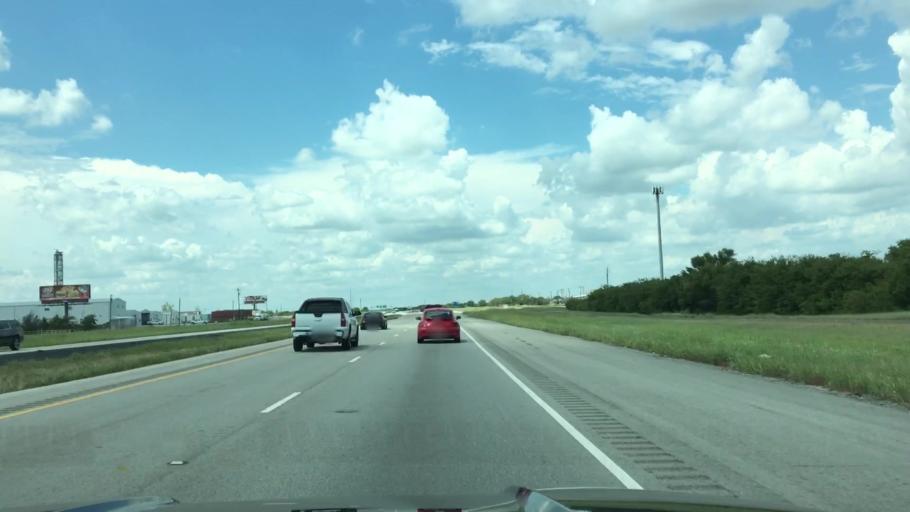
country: US
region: Texas
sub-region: Wise County
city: Rhome
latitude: 33.0329
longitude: -97.4499
